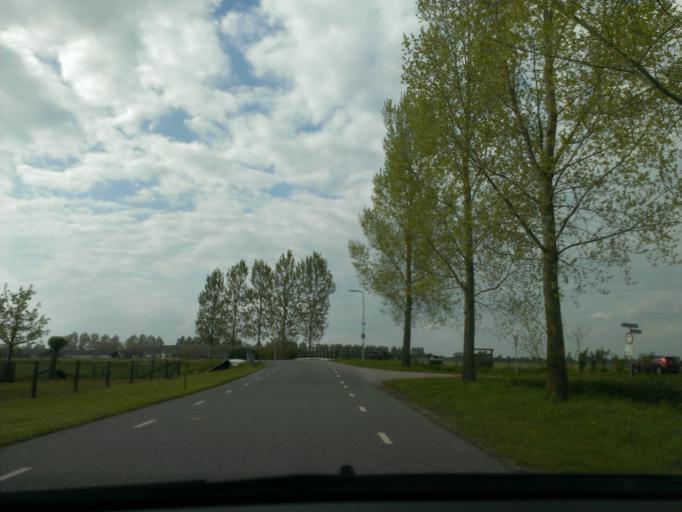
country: NL
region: Gelderland
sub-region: Gemeente Epe
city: Oene
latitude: 52.3302
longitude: 6.0604
